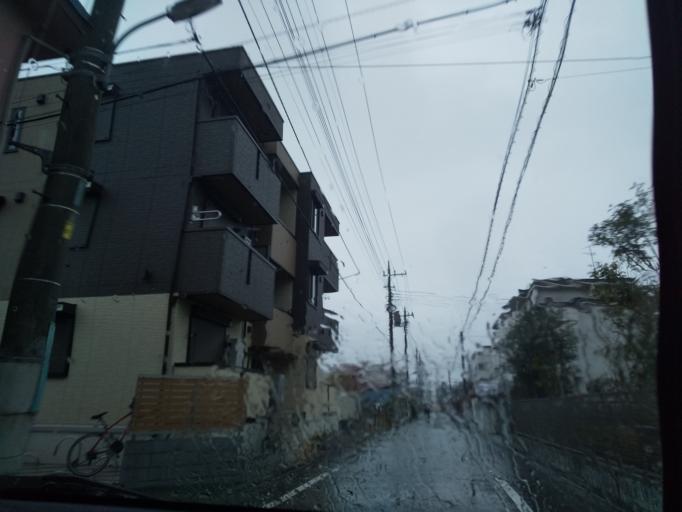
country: JP
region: Tokyo
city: Hino
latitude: 35.6930
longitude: 139.4157
